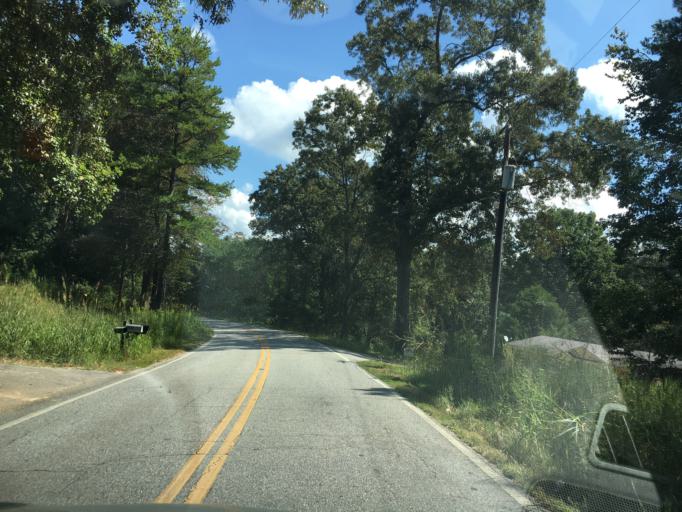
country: US
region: South Carolina
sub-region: Spartanburg County
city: Wellford
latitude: 34.8937
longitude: -82.0632
